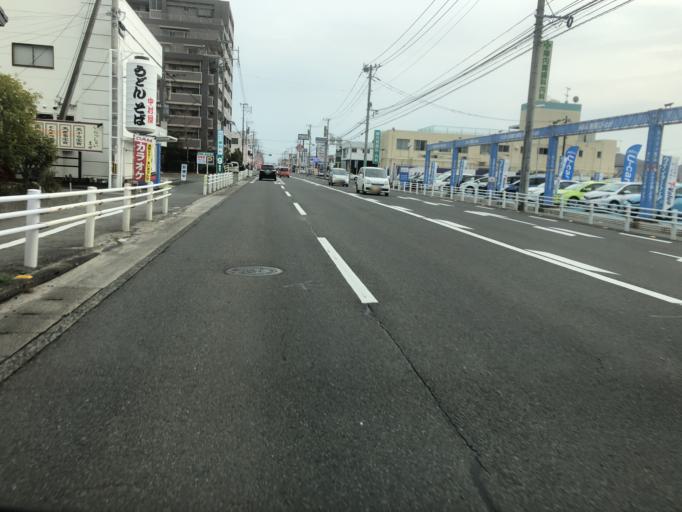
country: JP
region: Saga Prefecture
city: Saga-shi
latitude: 33.2546
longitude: 130.2741
